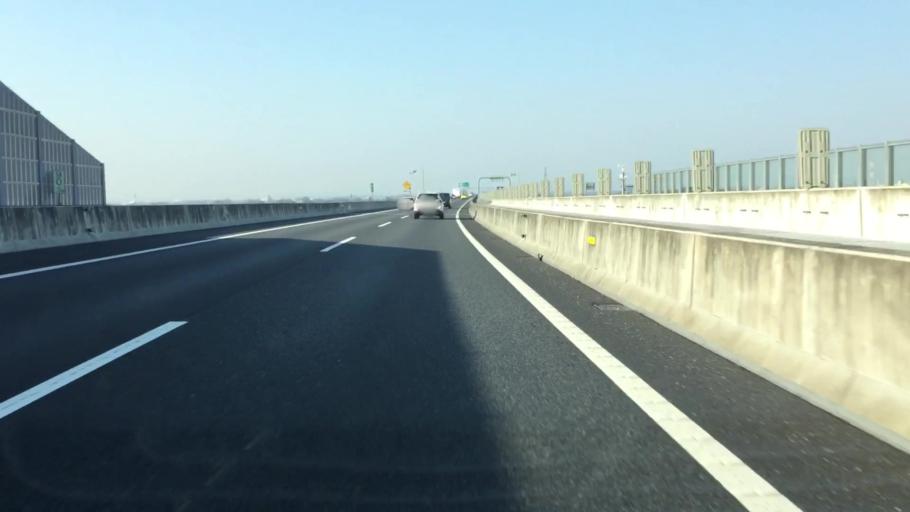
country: JP
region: Saitama
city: Okegawa
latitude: 35.9946
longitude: 139.5127
